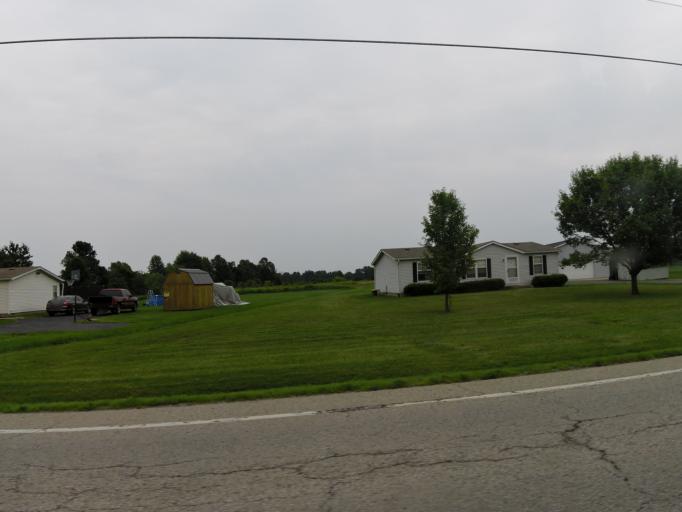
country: US
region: Ohio
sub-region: Brown County
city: Mount Orab
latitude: 39.1136
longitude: -83.9327
